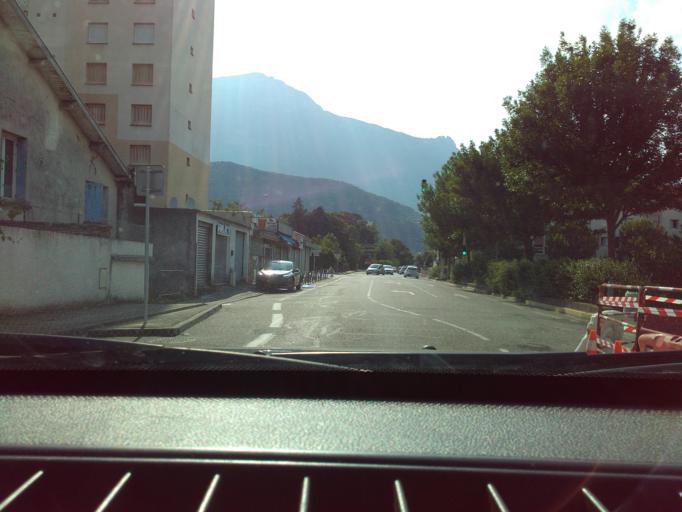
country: FR
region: Rhone-Alpes
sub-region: Departement de l'Isere
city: Grenoble
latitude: 45.1490
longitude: 5.7028
